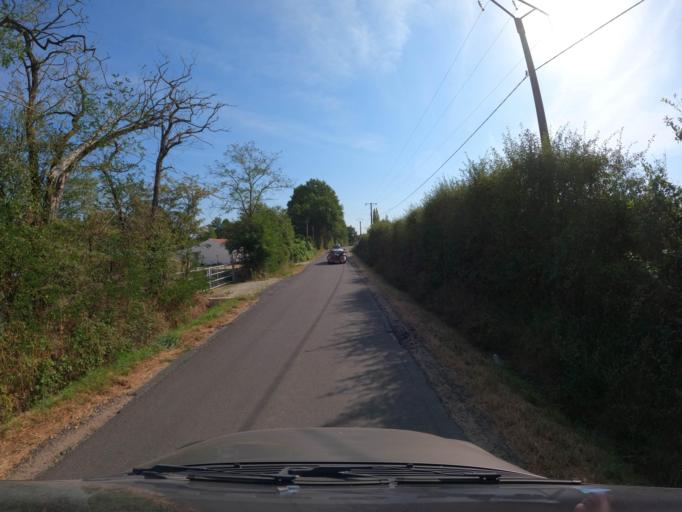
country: FR
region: Pays de la Loire
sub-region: Departement de la Vendee
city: Challans
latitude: 46.8094
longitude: -1.8437
